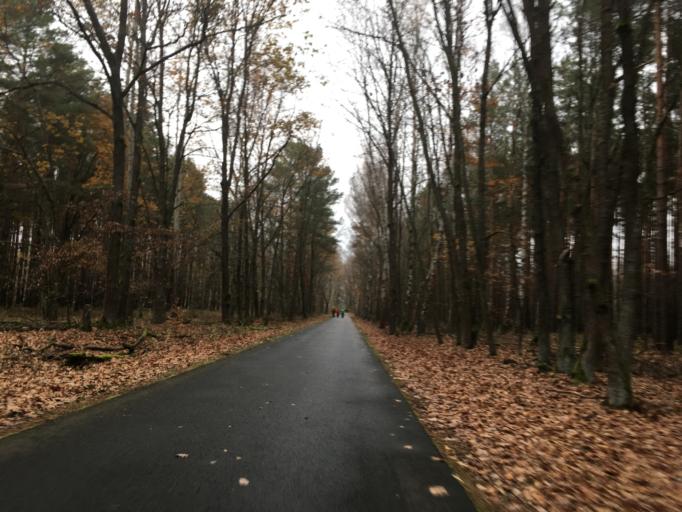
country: DE
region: Brandenburg
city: Mullrose
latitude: 52.2394
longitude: 14.4498
